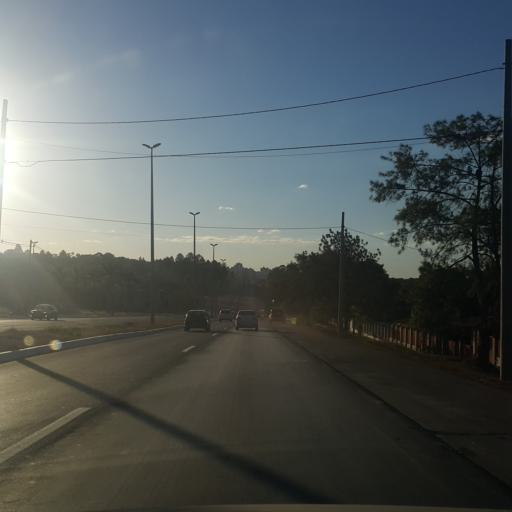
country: BR
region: Federal District
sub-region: Brasilia
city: Brasilia
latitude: -15.8629
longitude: -47.9840
